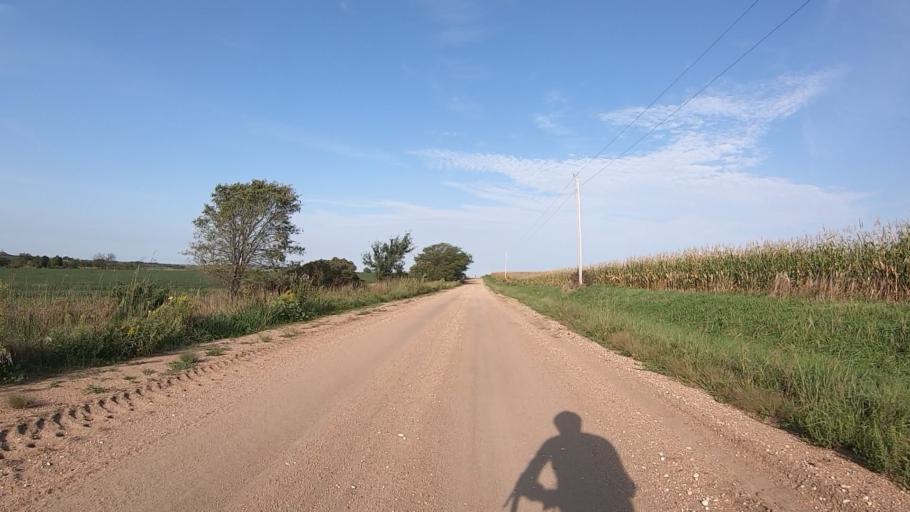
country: US
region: Kansas
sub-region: Marshall County
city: Blue Rapids
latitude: 39.6533
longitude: -96.8464
